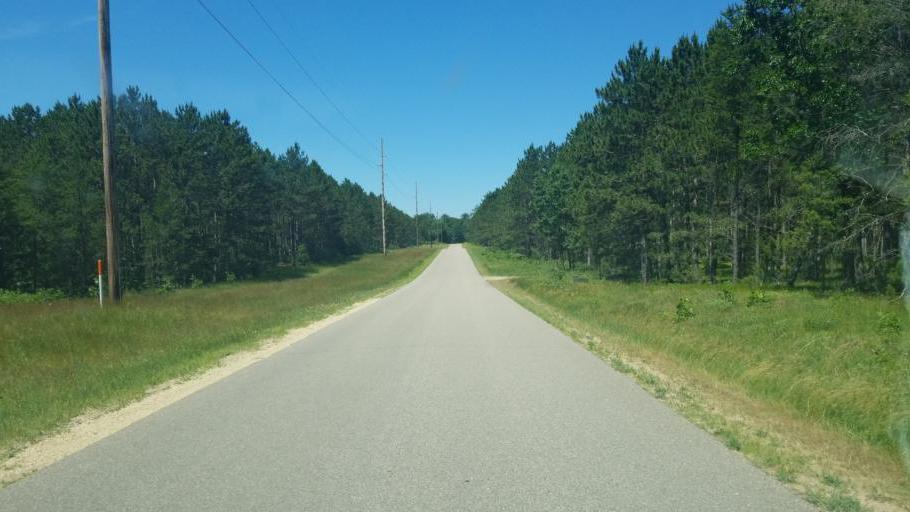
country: US
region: Wisconsin
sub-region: Adams County
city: Friendship
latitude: 43.9816
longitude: -89.9479
